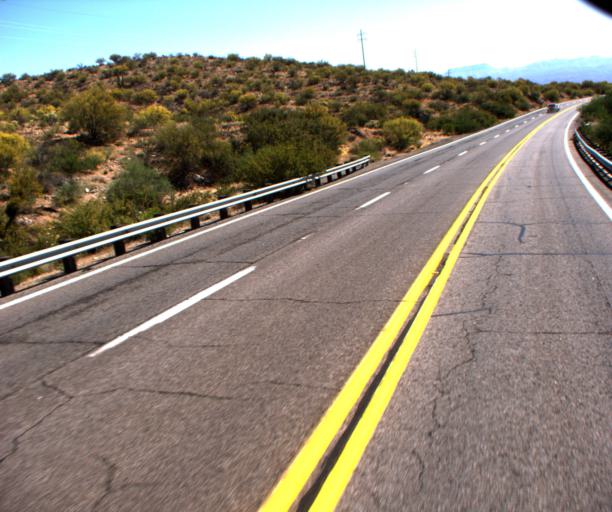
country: US
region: Arizona
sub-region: Pinal County
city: Mammoth
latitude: 32.6585
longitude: -110.6981
